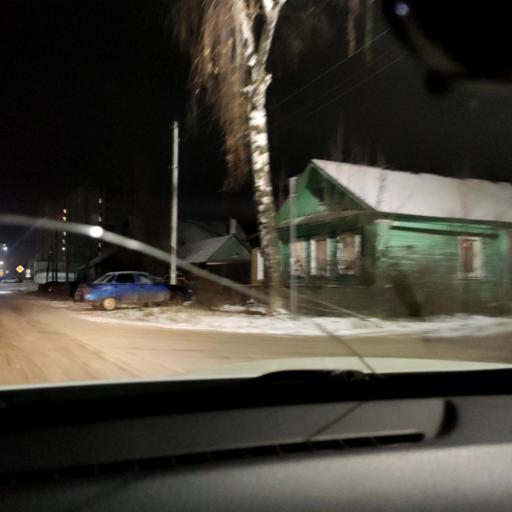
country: RU
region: Tatarstan
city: Staroye Arakchino
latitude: 55.8689
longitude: 49.0506
